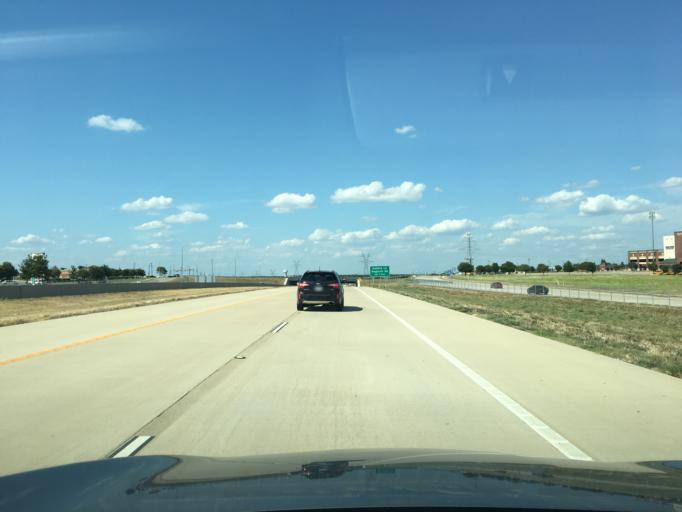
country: US
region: Texas
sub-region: Tarrant County
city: Mansfield
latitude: 32.5727
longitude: -97.0816
